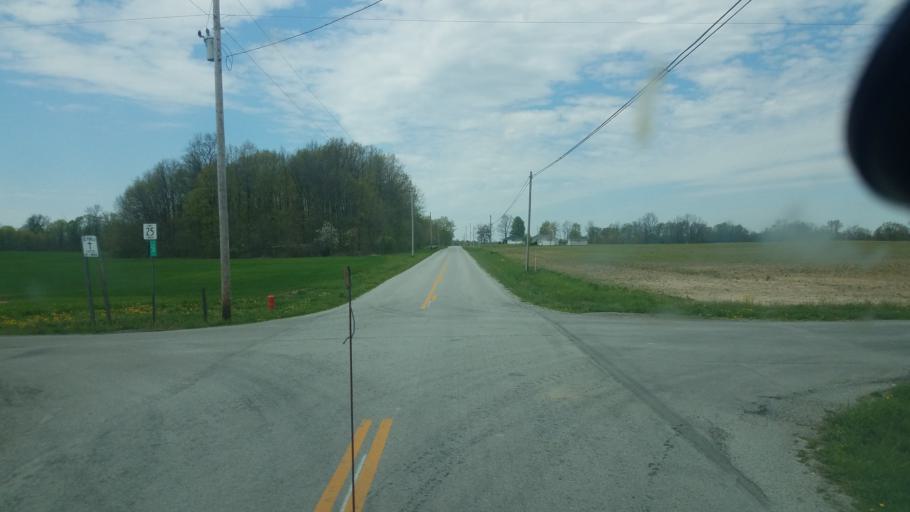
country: US
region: Ohio
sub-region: Hardin County
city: Ada
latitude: 40.7620
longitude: -83.8614
